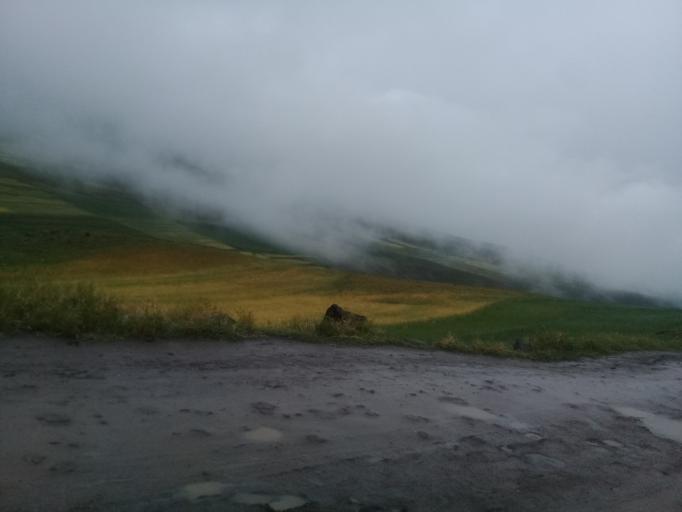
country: LS
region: Mokhotlong
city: Mokhotlong
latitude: -29.3842
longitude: 28.9802
